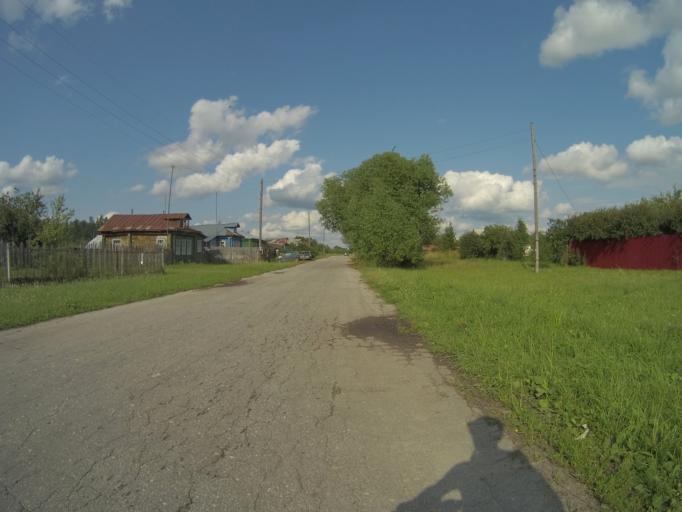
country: RU
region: Vladimir
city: Orgtrud
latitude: 56.2842
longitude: 40.7654
